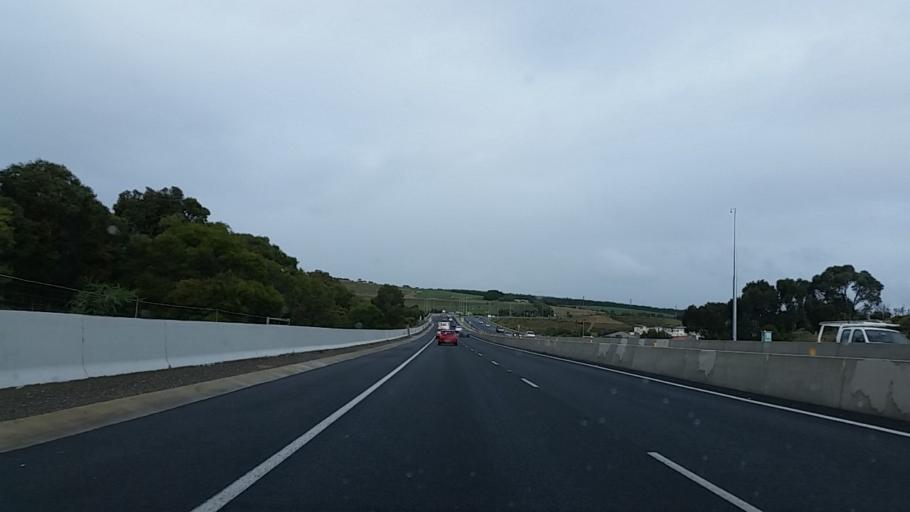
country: AU
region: South Australia
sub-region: Onkaparinga
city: Noarlunga Downs
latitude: -35.1599
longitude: 138.5069
